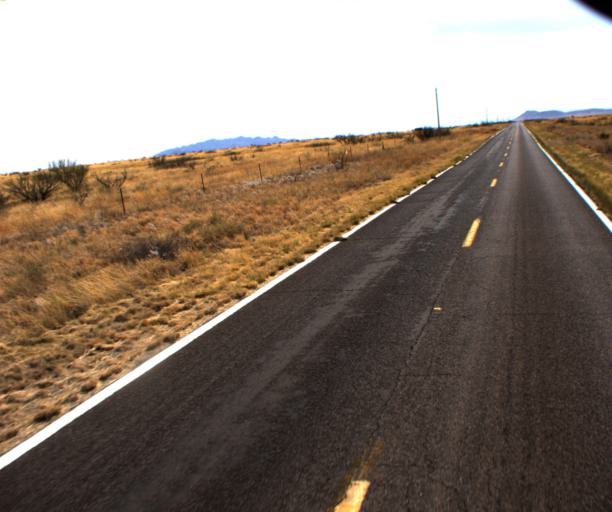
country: US
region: Arizona
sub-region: Cochise County
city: Willcox
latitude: 31.9412
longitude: -109.4855
